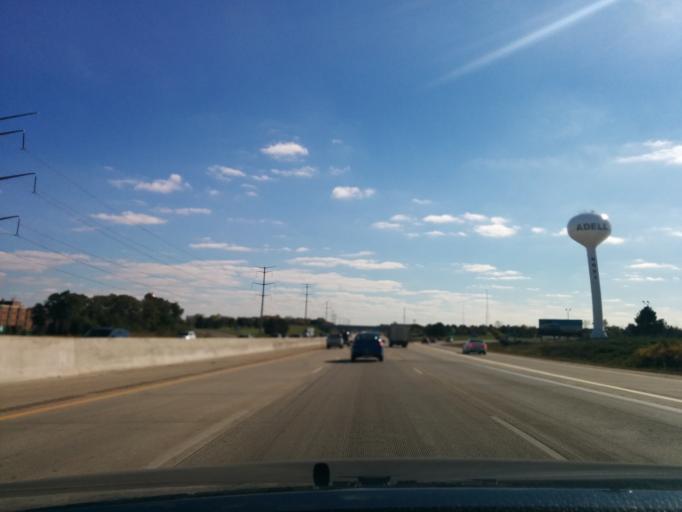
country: US
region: Michigan
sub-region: Oakland County
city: Novi
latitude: 42.4875
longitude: -83.4829
